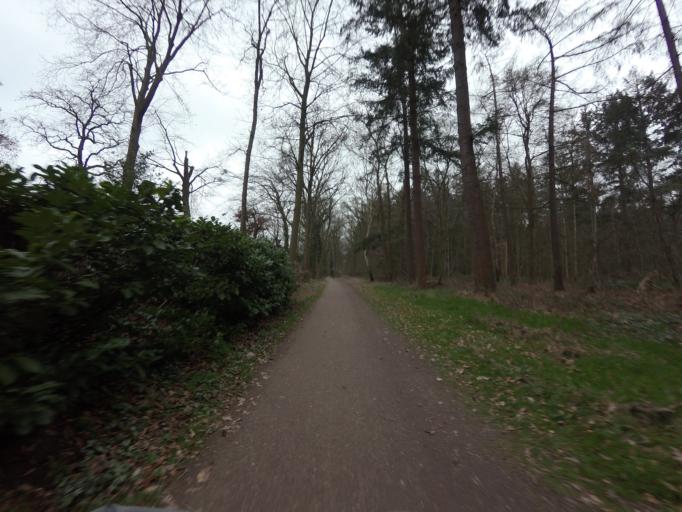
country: NL
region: North Holland
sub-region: Gemeente Hilversum
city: Hilversum
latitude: 52.2357
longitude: 5.1429
